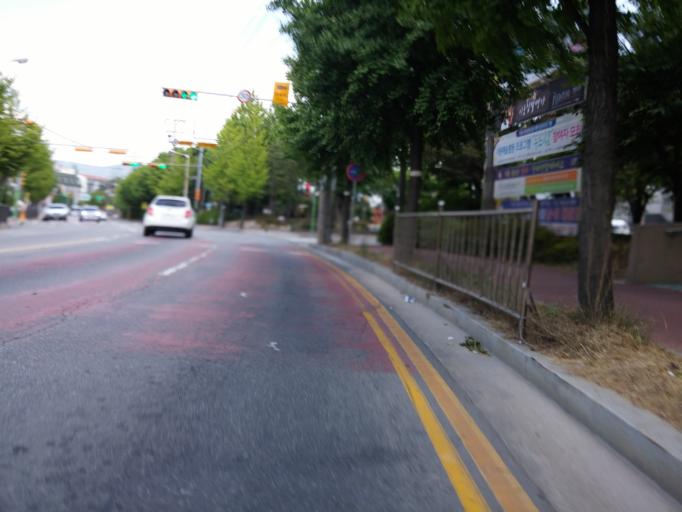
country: KR
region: Chungcheongbuk-do
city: Cheongju-si
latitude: 36.6177
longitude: 127.4764
